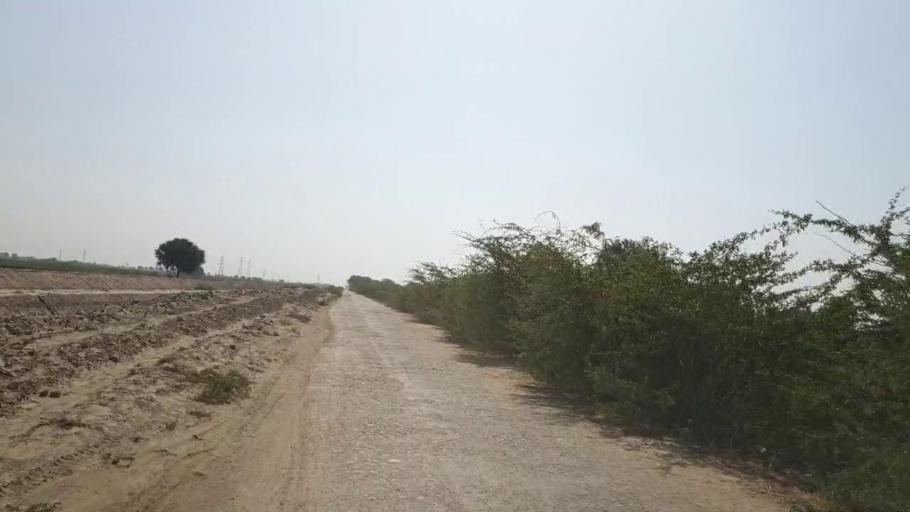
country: PK
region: Sindh
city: Naukot
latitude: 25.0125
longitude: 69.4561
